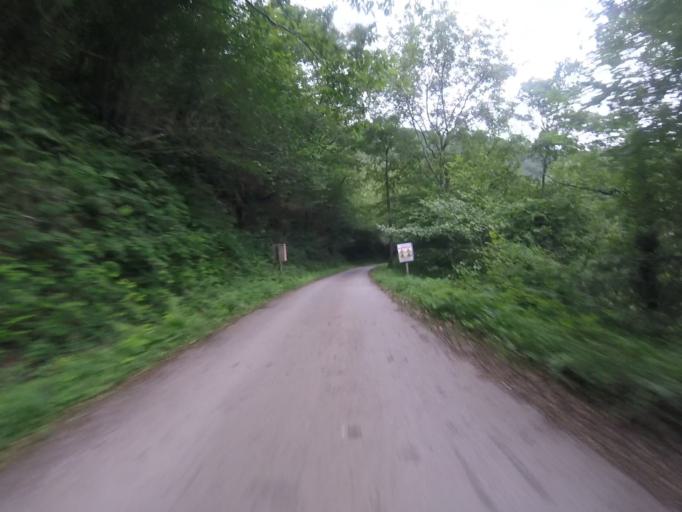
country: ES
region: Navarre
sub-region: Provincia de Navarra
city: Igantzi
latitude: 43.2177
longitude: -1.6790
